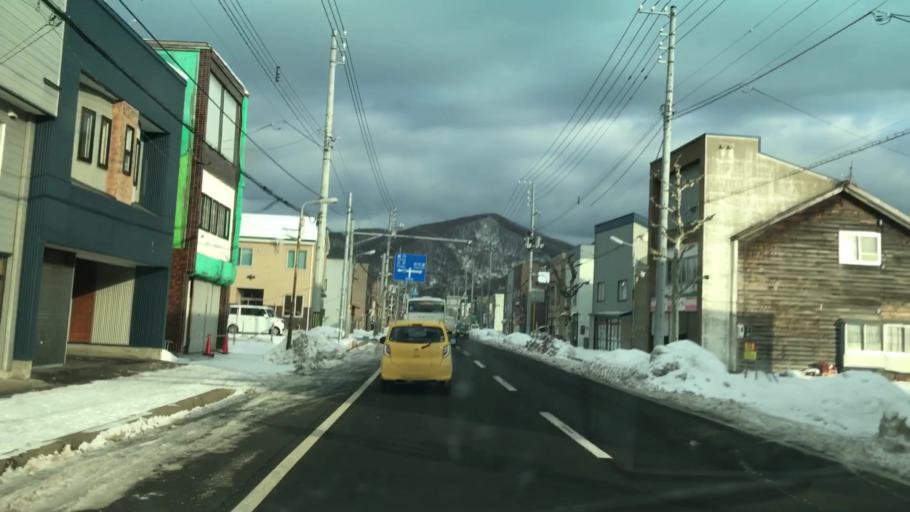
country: JP
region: Hokkaido
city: Yoichi
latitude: 43.2046
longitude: 140.7714
